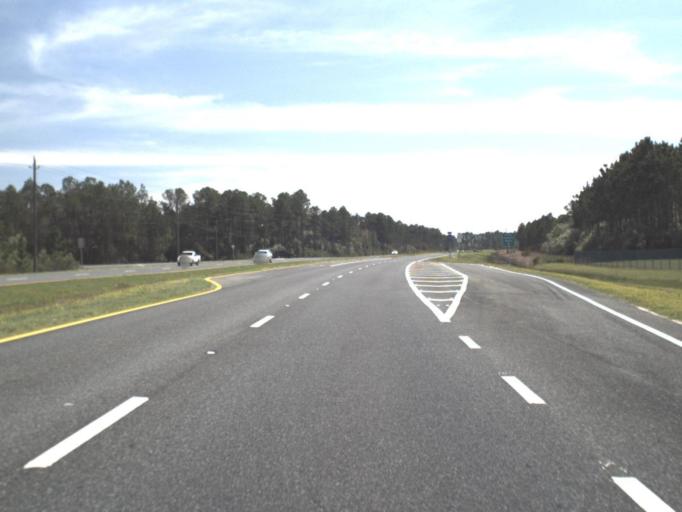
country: US
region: Florida
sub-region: Bay County
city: Lynn Haven
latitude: 30.3379
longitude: -85.6601
